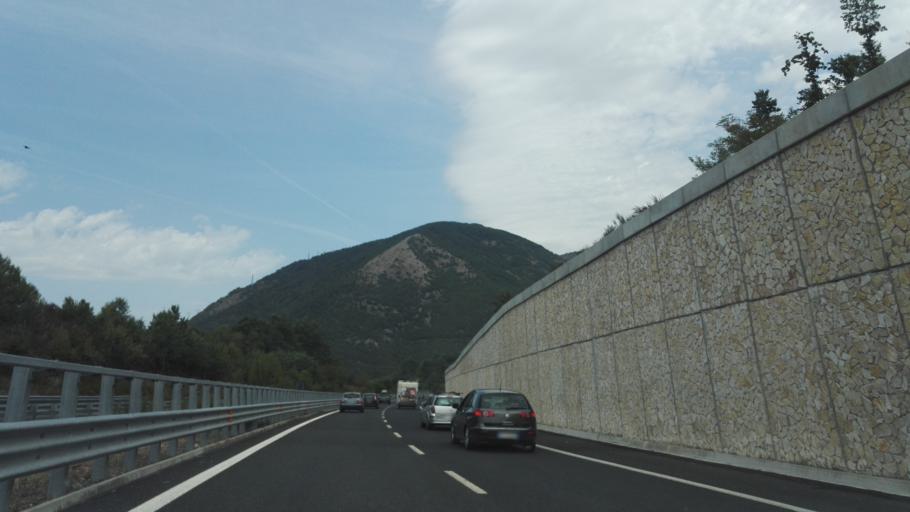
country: IT
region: Basilicate
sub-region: Provincia di Potenza
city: Lagonegro
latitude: 40.1160
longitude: 15.7852
